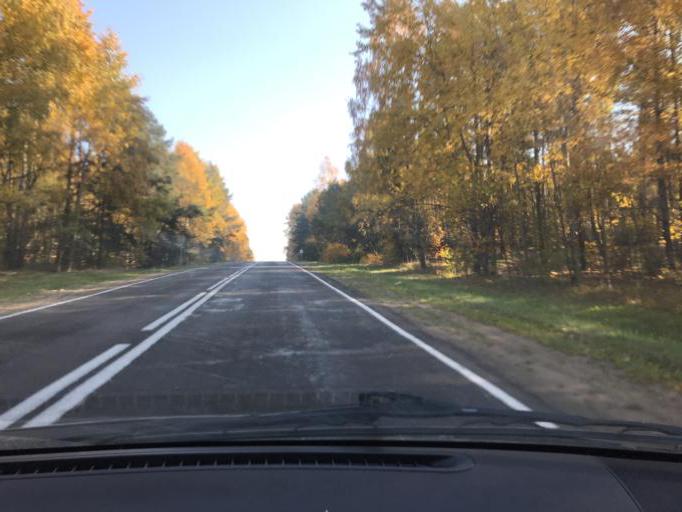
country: BY
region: Brest
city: Baranovichi
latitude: 52.9303
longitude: 26.0309
